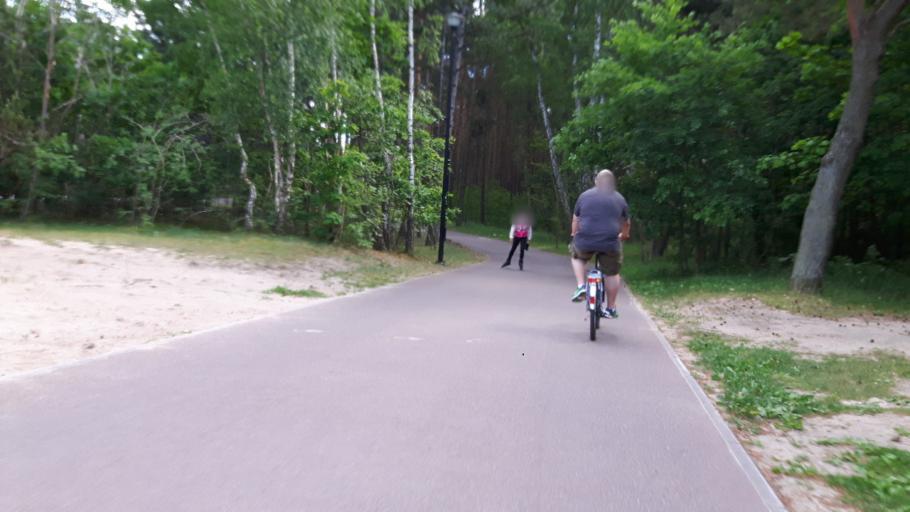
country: PL
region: Pomeranian Voivodeship
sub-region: Sopot
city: Sopot
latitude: 54.4191
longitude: 18.6098
